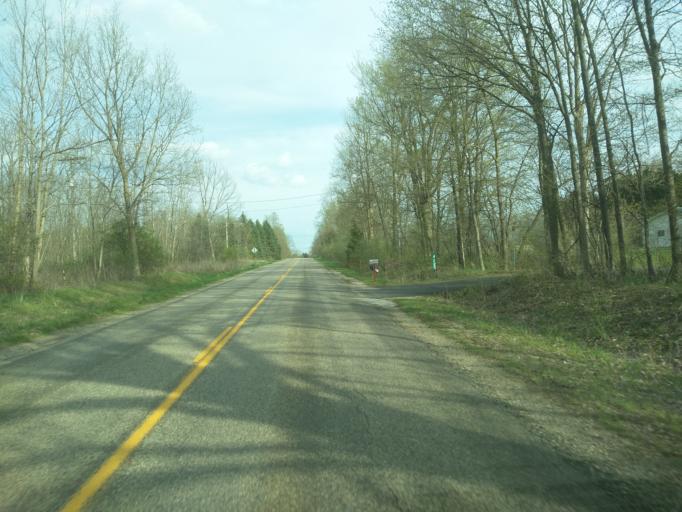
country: US
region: Michigan
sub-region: Eaton County
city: Dimondale
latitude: 42.6380
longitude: -84.6462
